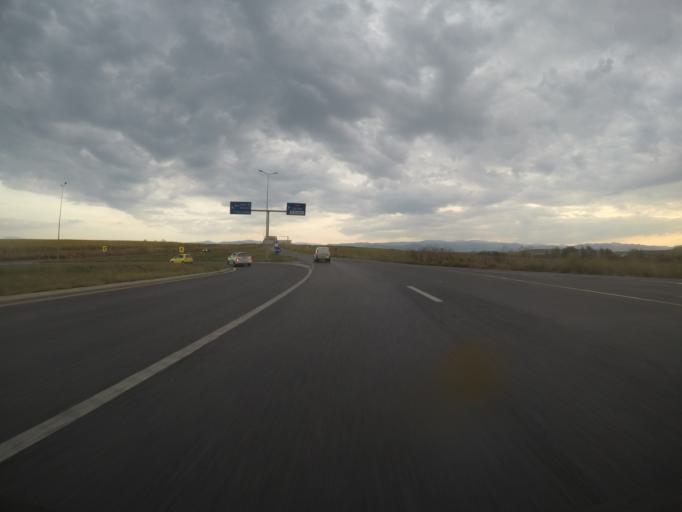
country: RO
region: Sibiu
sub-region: Comuna Sura Mica
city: Sura Mica
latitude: 45.8154
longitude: 24.0732
